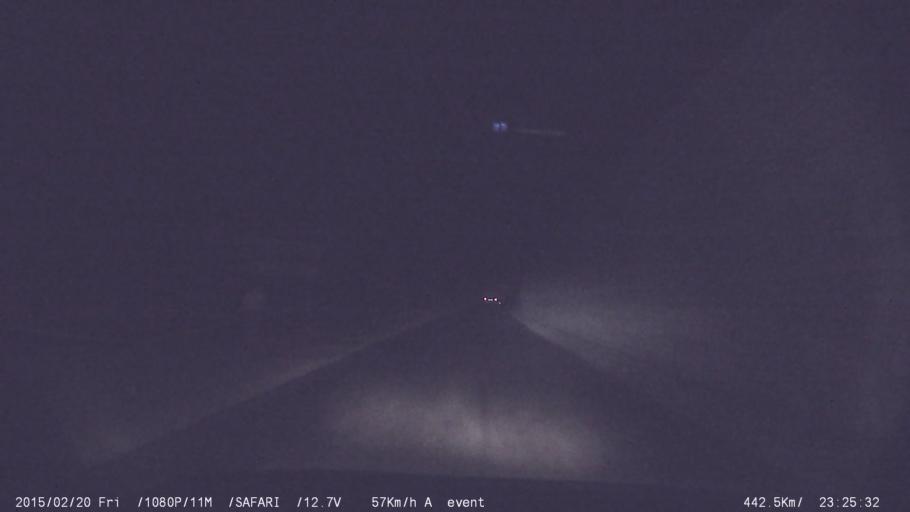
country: IN
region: Kerala
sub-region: Palakkad district
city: Palakkad
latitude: 10.7719
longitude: 76.6925
